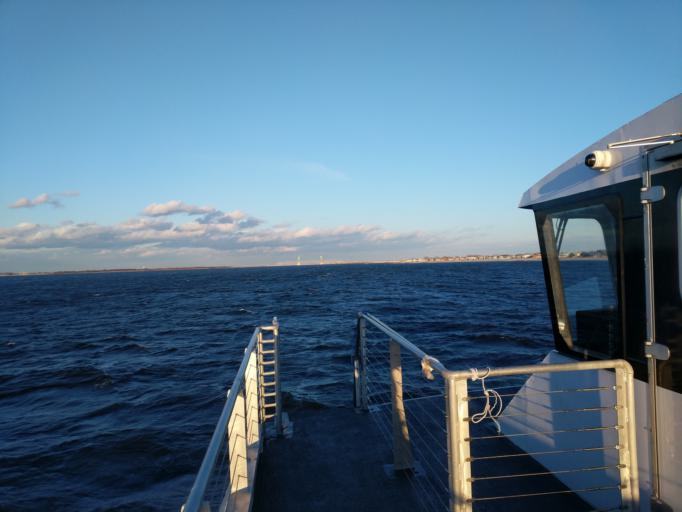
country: US
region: New York
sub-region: Kings County
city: Coney Island
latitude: 40.5631
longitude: -73.9314
